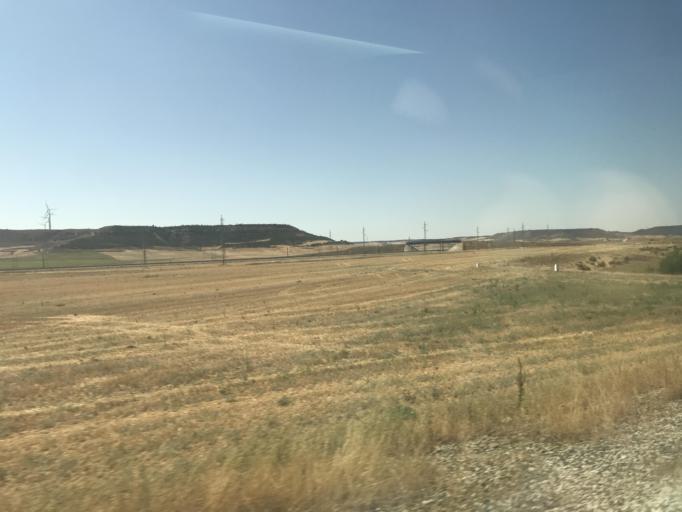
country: ES
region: Castille and Leon
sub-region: Provincia de Palencia
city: Torquemada
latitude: 42.0090
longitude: -4.3139
